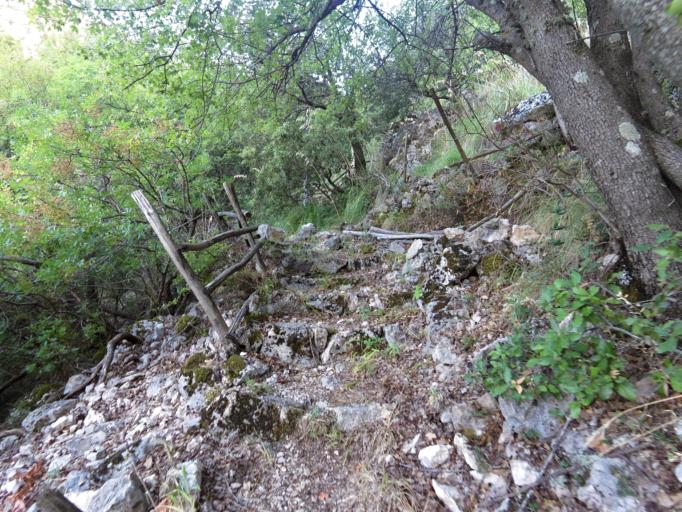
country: IT
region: Calabria
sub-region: Provincia di Reggio Calabria
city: Pazzano
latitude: 38.4723
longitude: 16.4502
